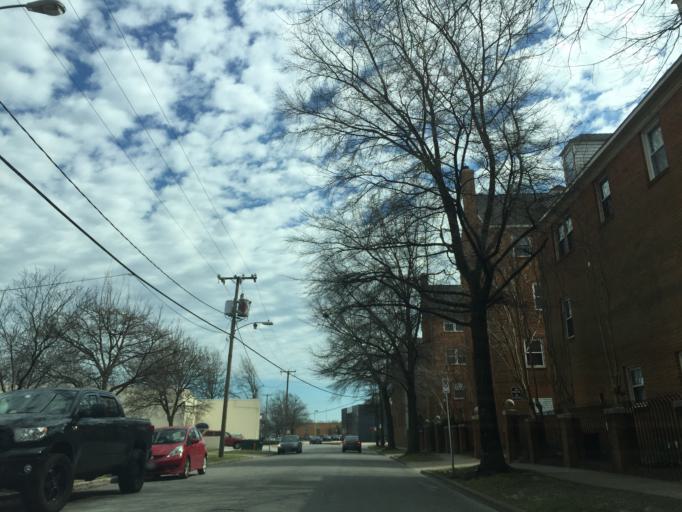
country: US
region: Virginia
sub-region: City of Norfolk
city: Norfolk
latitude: 36.8687
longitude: -76.2934
